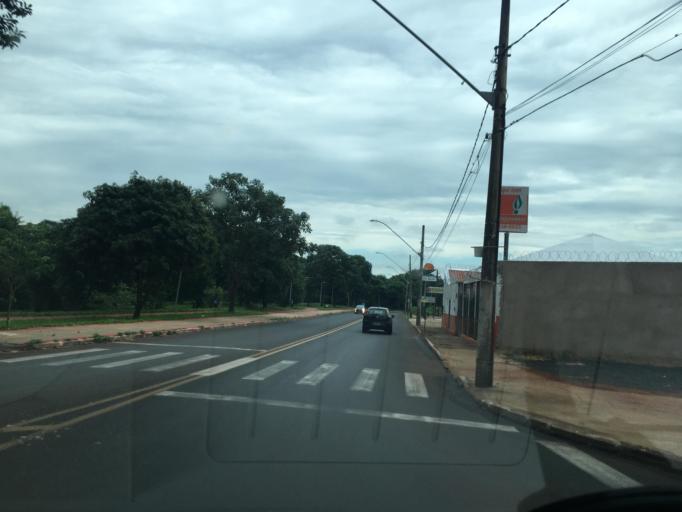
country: BR
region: Minas Gerais
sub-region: Uberlandia
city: Uberlandia
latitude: -18.9202
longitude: -48.3026
